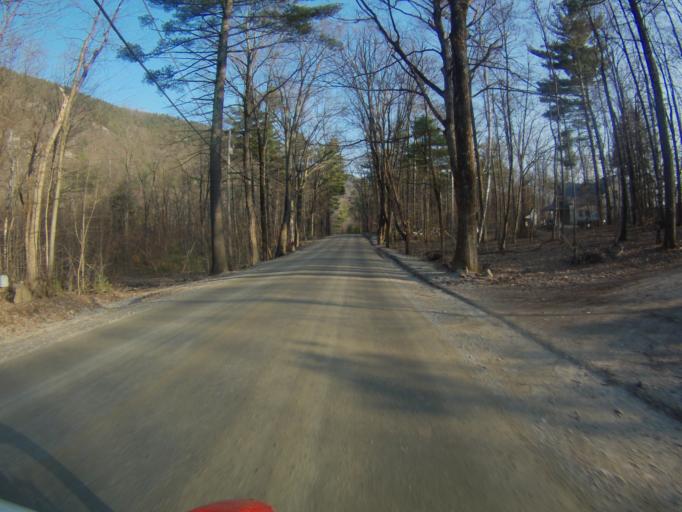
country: US
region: Vermont
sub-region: Addison County
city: Bristol
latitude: 44.1156
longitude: -73.0783
